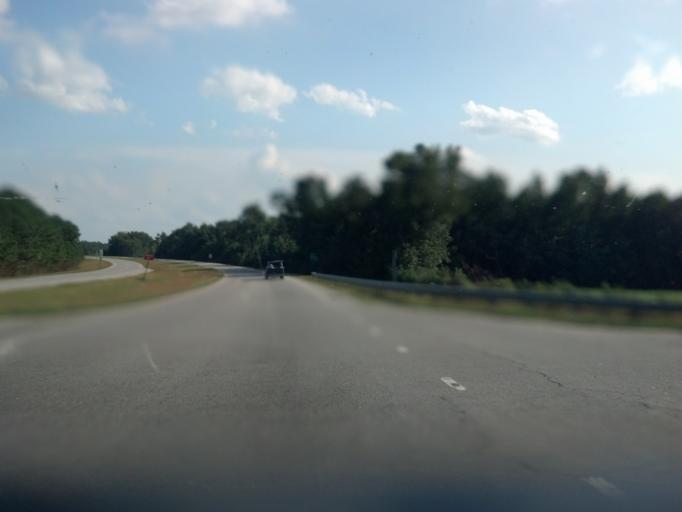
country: US
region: North Carolina
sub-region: Pitt County
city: Bethel
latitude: 35.8312
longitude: -77.3743
